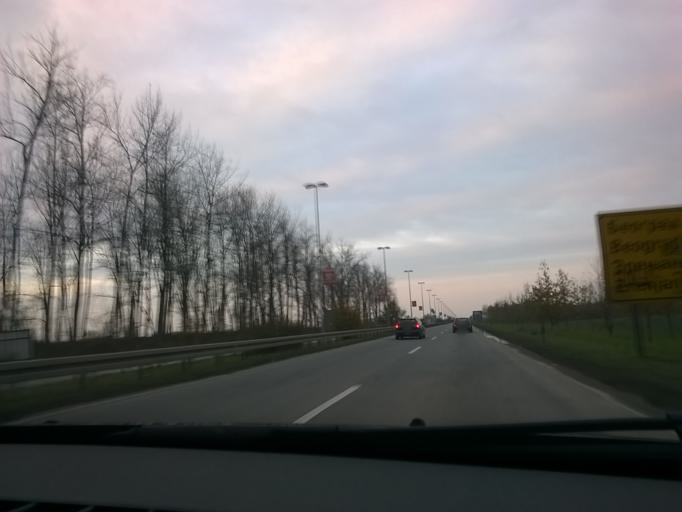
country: RS
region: Autonomna Pokrajina Vojvodina
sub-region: Juznobacki Okrug
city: Novi Sad
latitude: 45.2825
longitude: 19.8513
